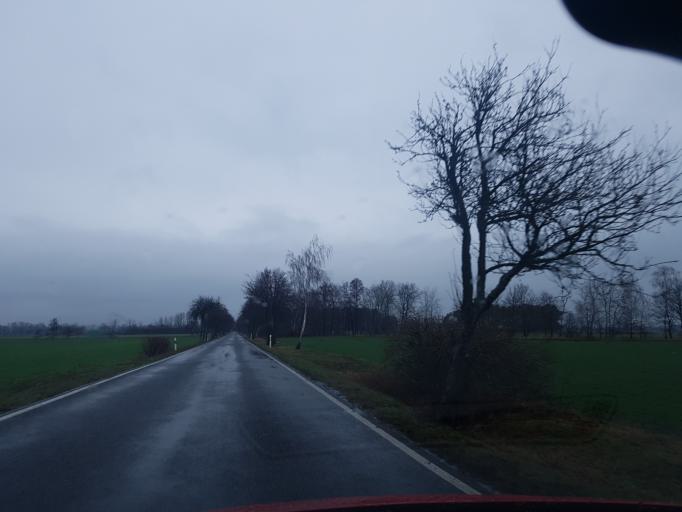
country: DE
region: Brandenburg
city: Schilda
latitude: 51.6120
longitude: 13.3186
